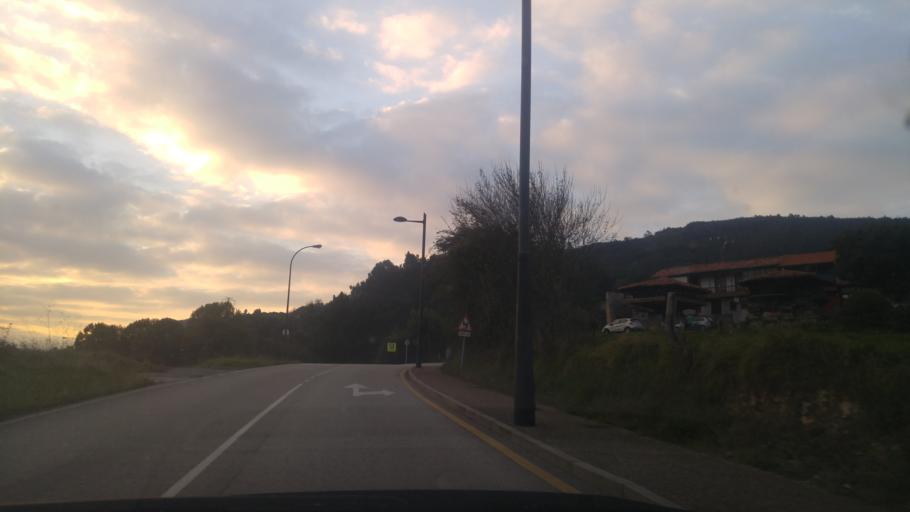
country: ES
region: Asturias
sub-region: Province of Asturias
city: Oviedo
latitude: 43.3762
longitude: -5.8650
